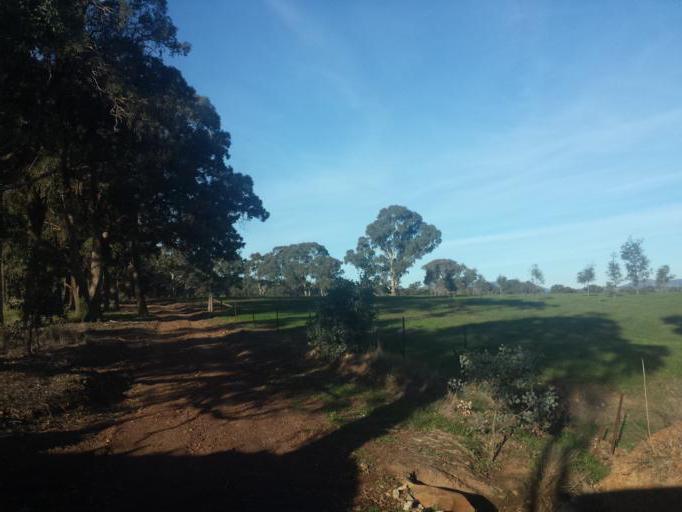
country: AU
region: Victoria
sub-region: Murrindindi
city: Kinglake West
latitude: -36.9997
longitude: 145.2264
